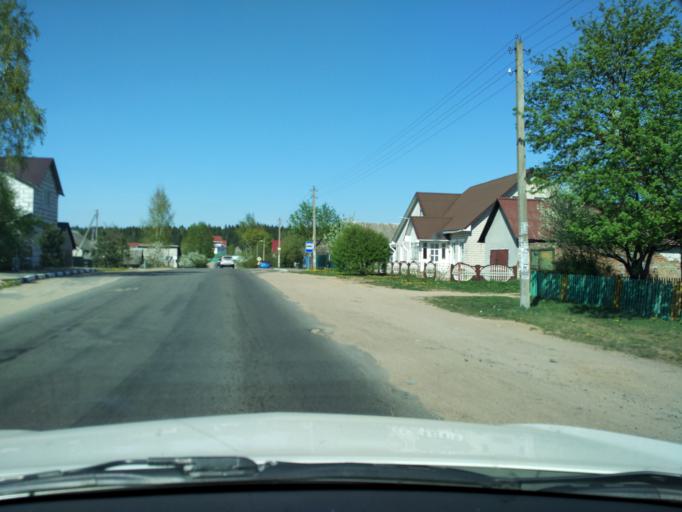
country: BY
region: Minsk
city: Lyeskawka
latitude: 54.0014
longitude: 27.7180
